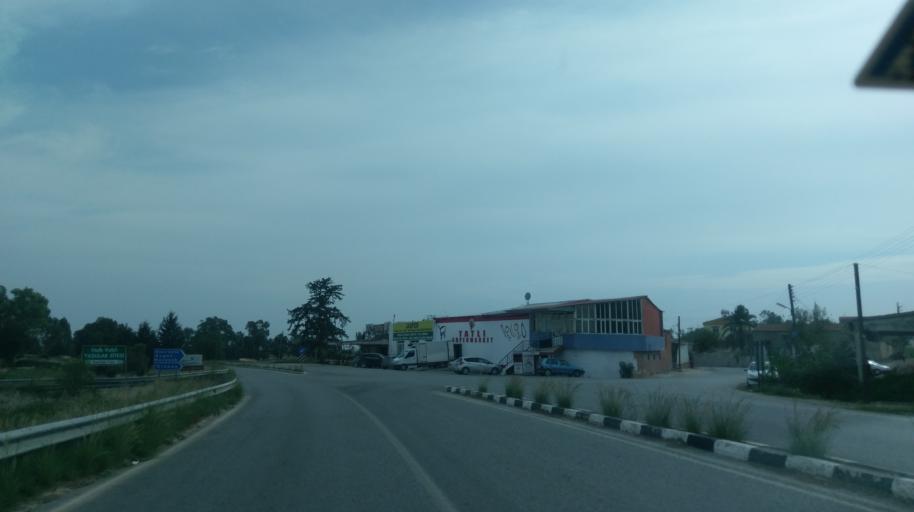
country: CY
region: Ammochostos
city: Trikomo
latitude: 35.2766
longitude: 33.8519
